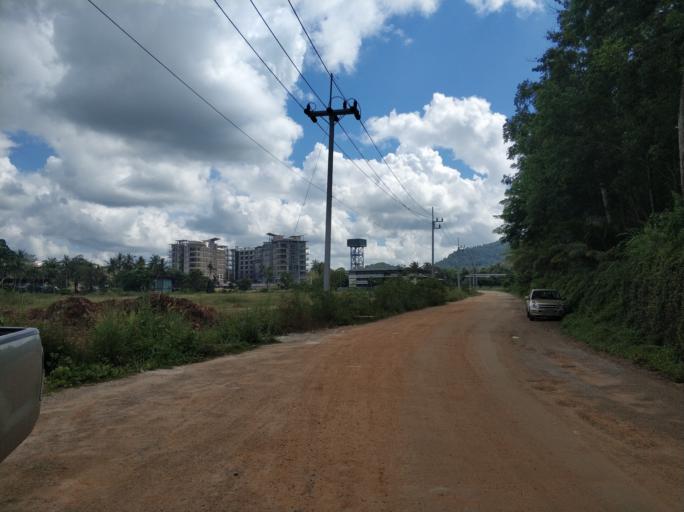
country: TH
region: Phangnga
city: Ban Ao Nang
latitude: 8.0303
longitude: 98.8270
